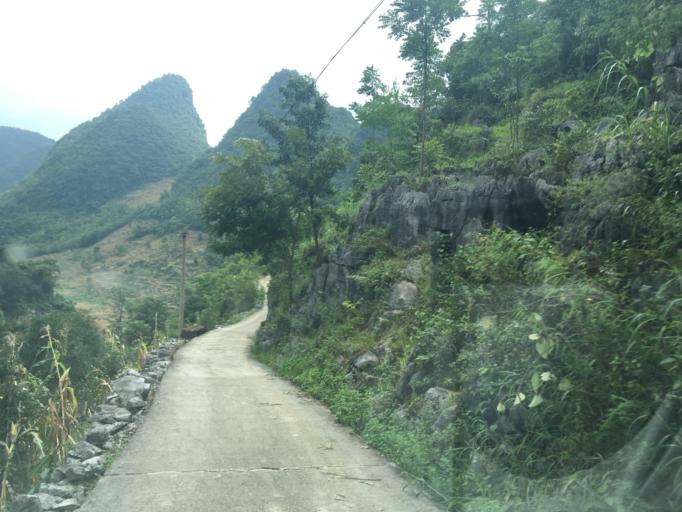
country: CN
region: Guangxi Zhuangzu Zizhiqu
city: Xinzhou
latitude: 25.2274
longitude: 105.6402
